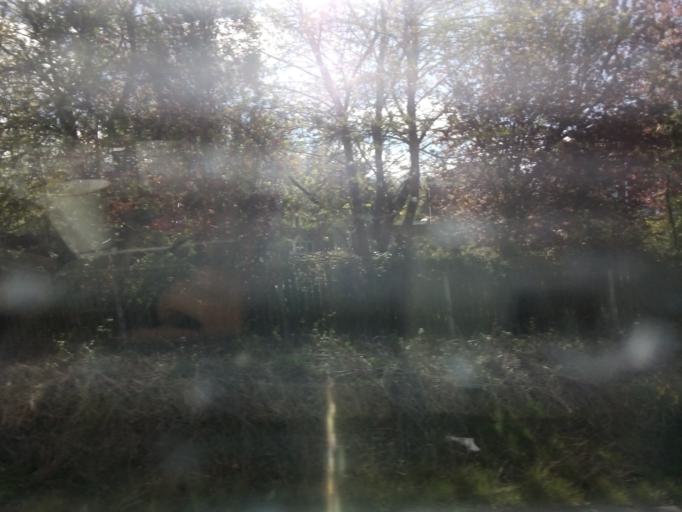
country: GB
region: England
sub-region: Northumberland
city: Morpeth
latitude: 55.1552
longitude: -1.6831
